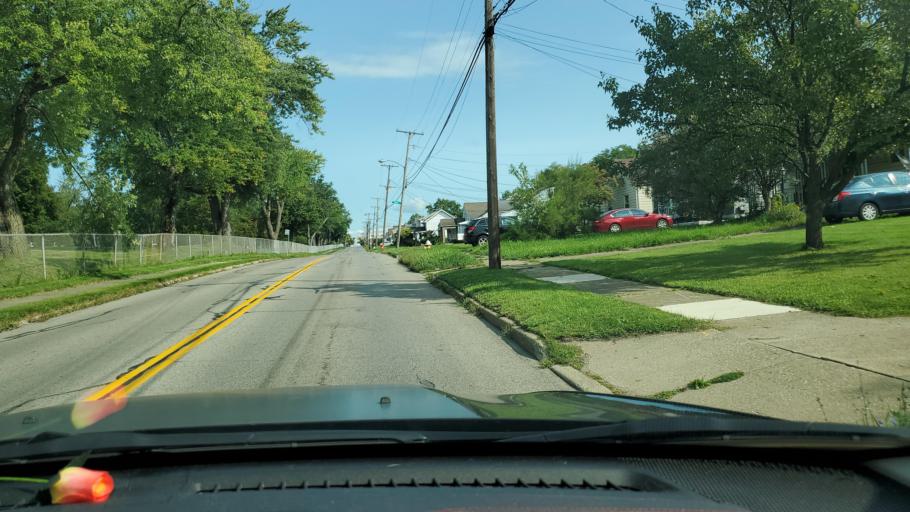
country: US
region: Ohio
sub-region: Mahoning County
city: Youngstown
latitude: 41.0983
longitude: -80.6887
